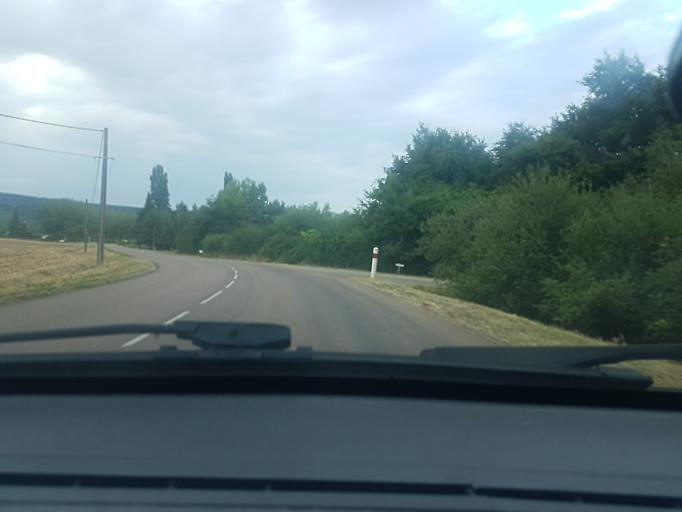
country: FR
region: Bourgogne
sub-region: Departement de Saone-et-Loire
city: Givry
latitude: 46.7625
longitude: 4.7445
